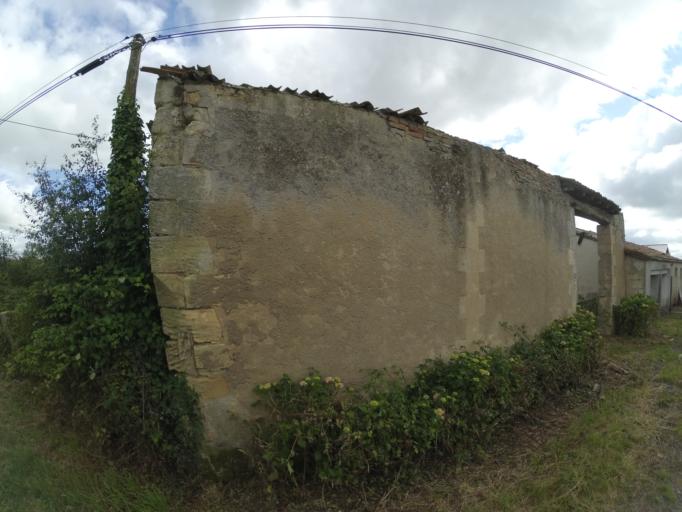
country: FR
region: Aquitaine
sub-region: Departement de la Gironde
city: Ludon-Medoc
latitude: 44.9942
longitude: -0.5899
